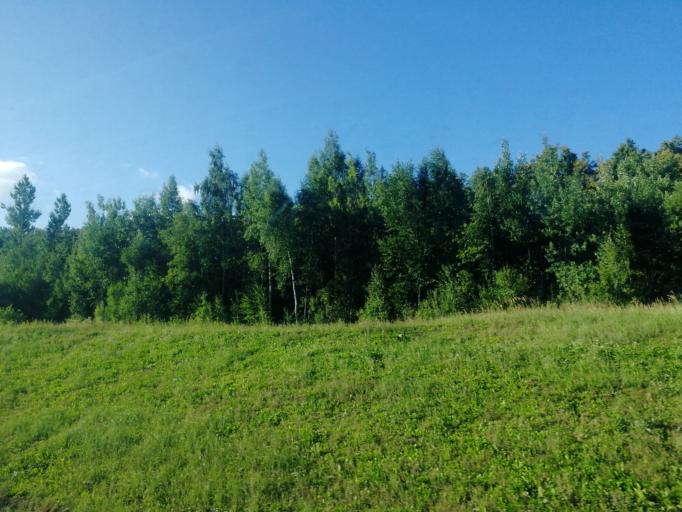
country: RU
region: Tula
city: Novogurovskiy
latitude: 54.2777
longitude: 37.2460
